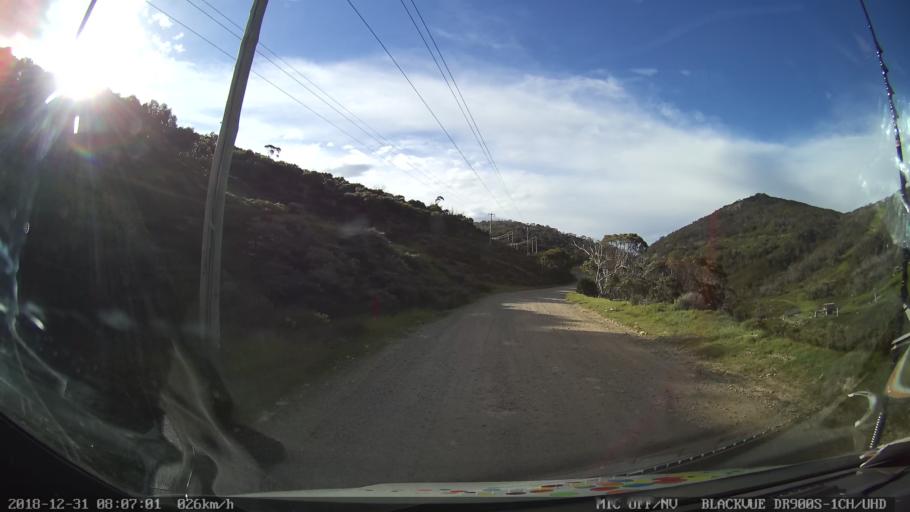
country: AU
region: New South Wales
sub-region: Snowy River
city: Jindabyne
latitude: -36.3768
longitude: 148.4087
